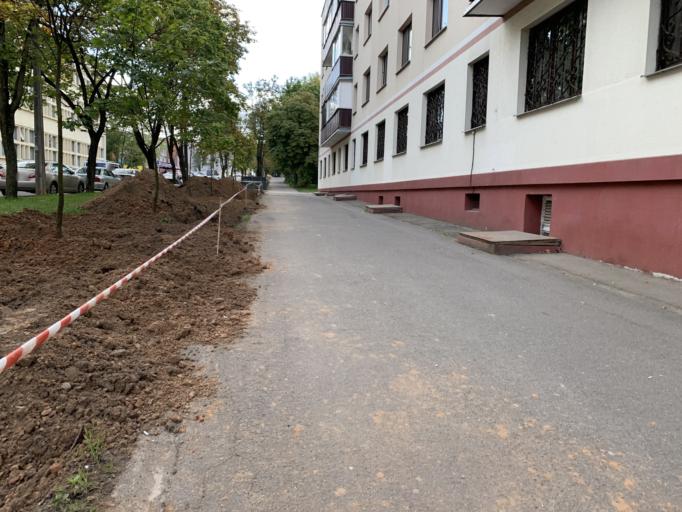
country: BY
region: Minsk
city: Minsk
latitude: 53.9145
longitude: 27.5899
